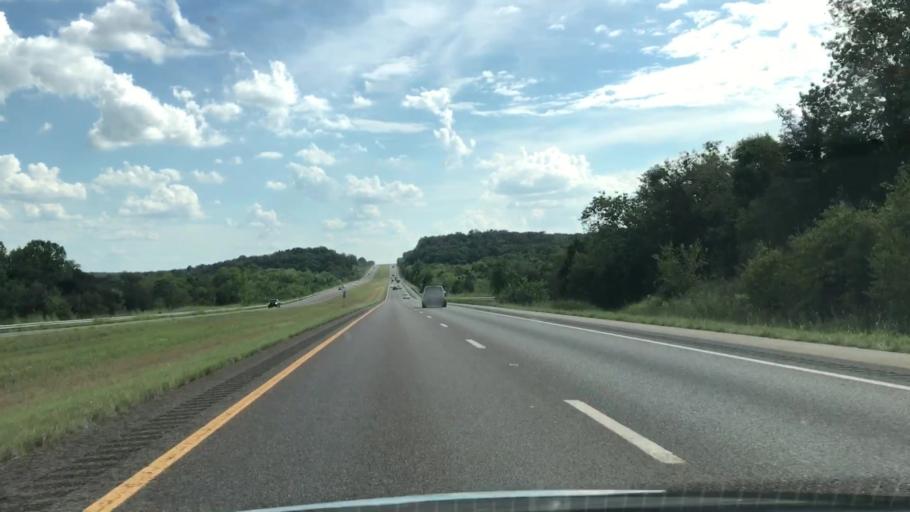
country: US
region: Tennessee
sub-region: Maury County
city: Columbia
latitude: 35.6084
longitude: -86.9010
